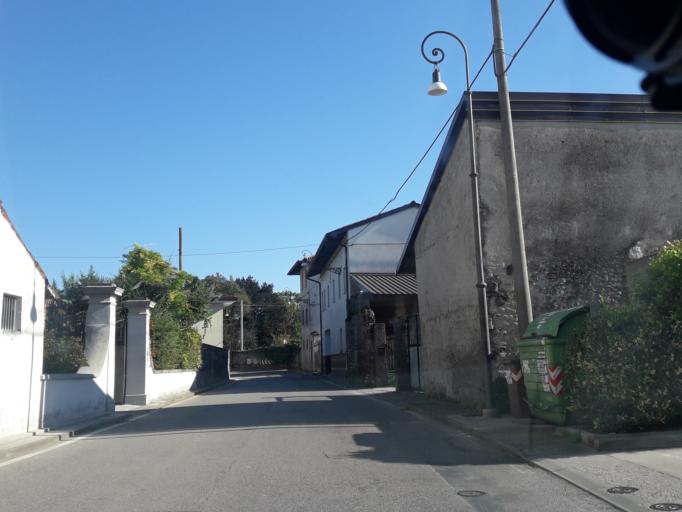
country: IT
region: Friuli Venezia Giulia
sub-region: Provincia di Udine
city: Povoletto
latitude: 46.1026
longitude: 13.2674
